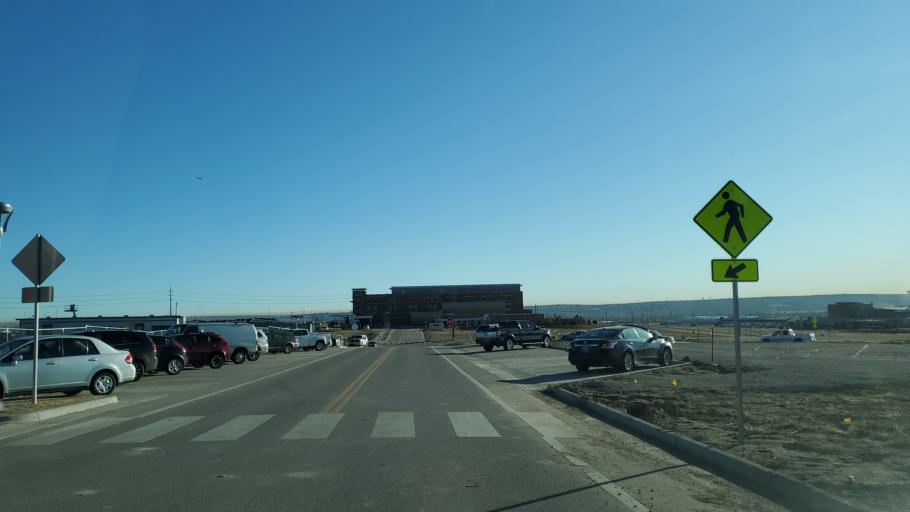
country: US
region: Colorado
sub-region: Broomfield County
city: Broomfield
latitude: 39.9105
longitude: -105.0956
